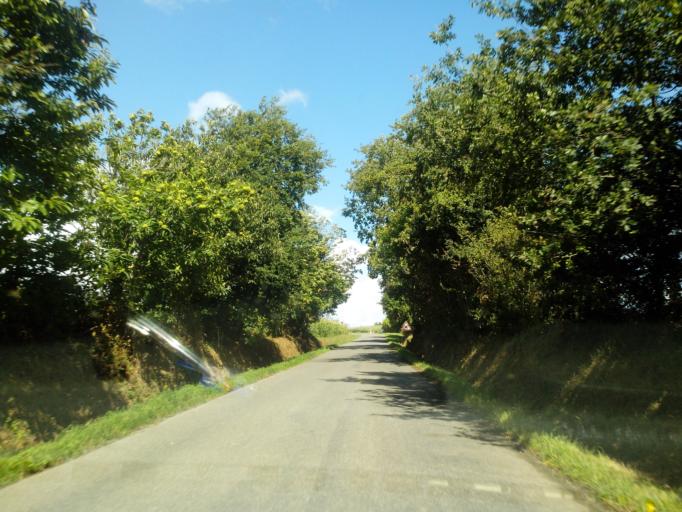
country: FR
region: Brittany
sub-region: Departement des Cotes-d'Armor
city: Merdrignac
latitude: 48.1764
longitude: -2.4162
